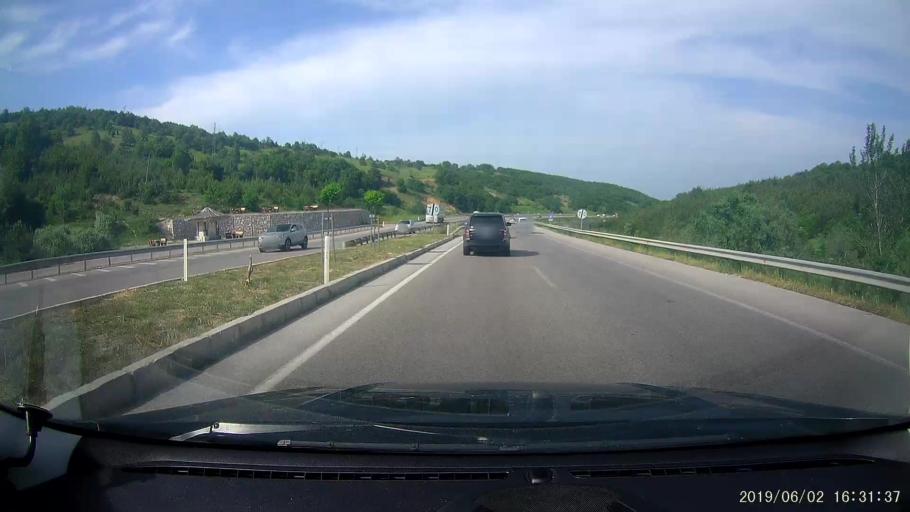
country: TR
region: Samsun
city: Ladik
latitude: 41.0337
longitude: 35.9035
